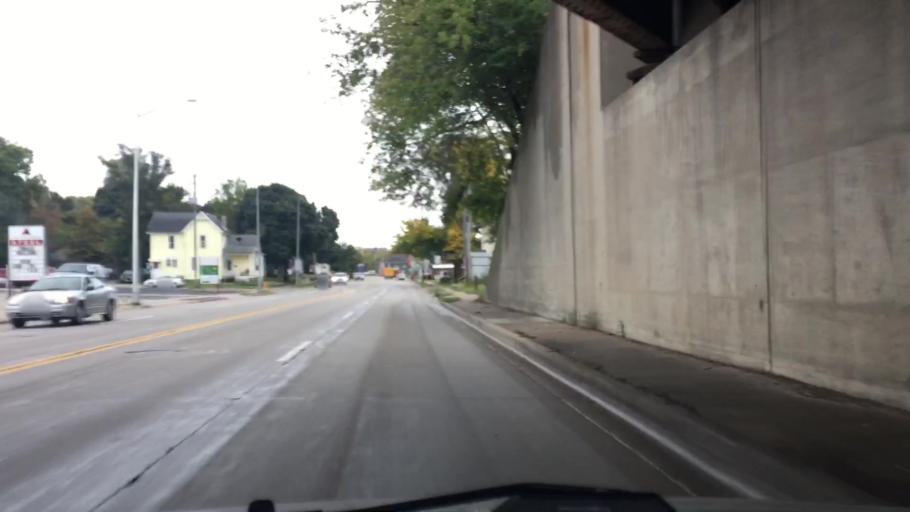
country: US
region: Wisconsin
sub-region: Rock County
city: Janesville
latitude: 42.6888
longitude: -89.0267
